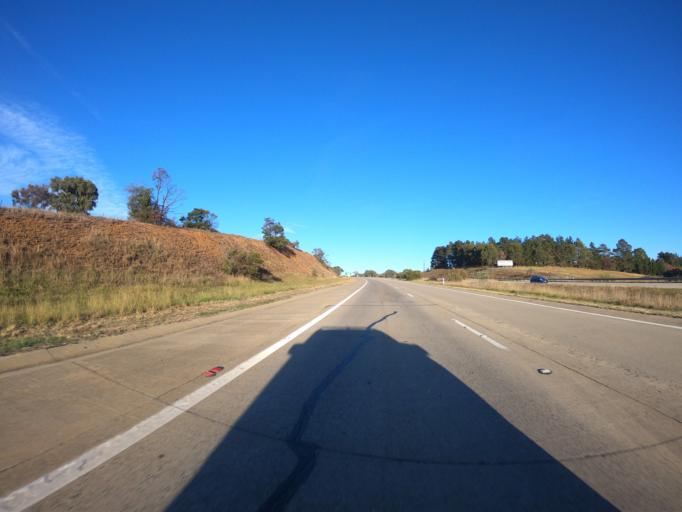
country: AU
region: New South Wales
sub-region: Yass Valley
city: Gundaroo
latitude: -35.1765
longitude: 149.2743
